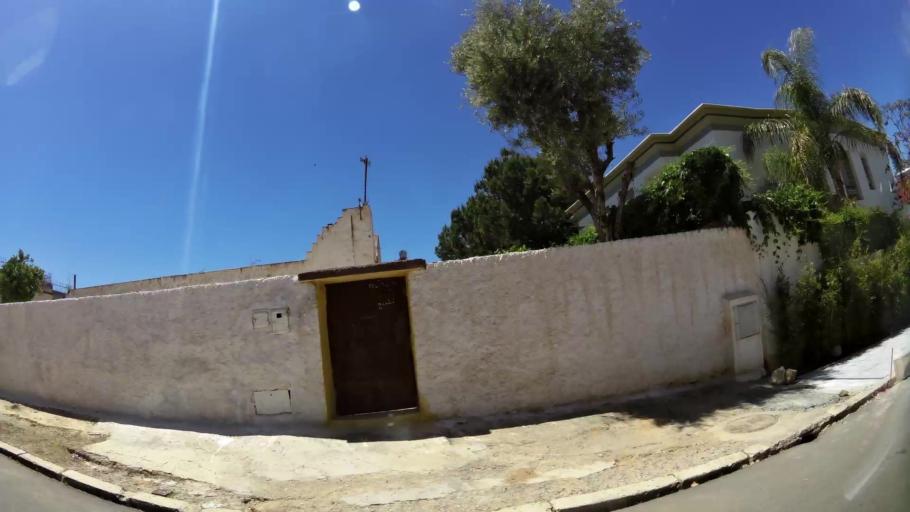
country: MA
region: Meknes-Tafilalet
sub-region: Meknes
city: Meknes
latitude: 33.9088
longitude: -5.5622
